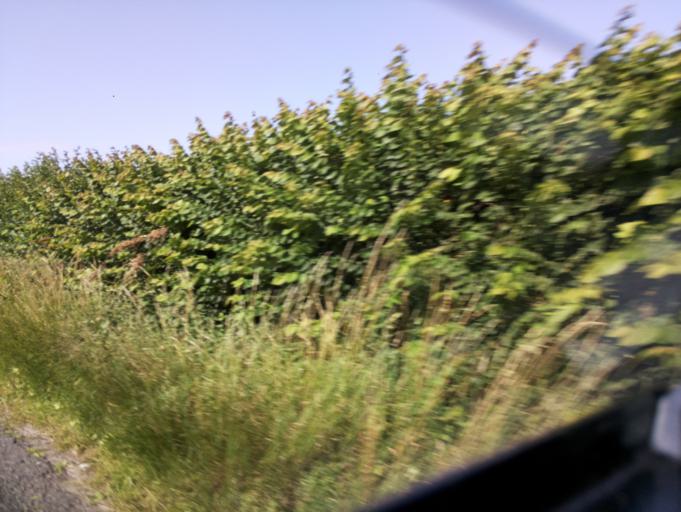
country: GB
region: England
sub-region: Oxfordshire
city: Ducklington
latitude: 51.7363
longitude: -1.5025
